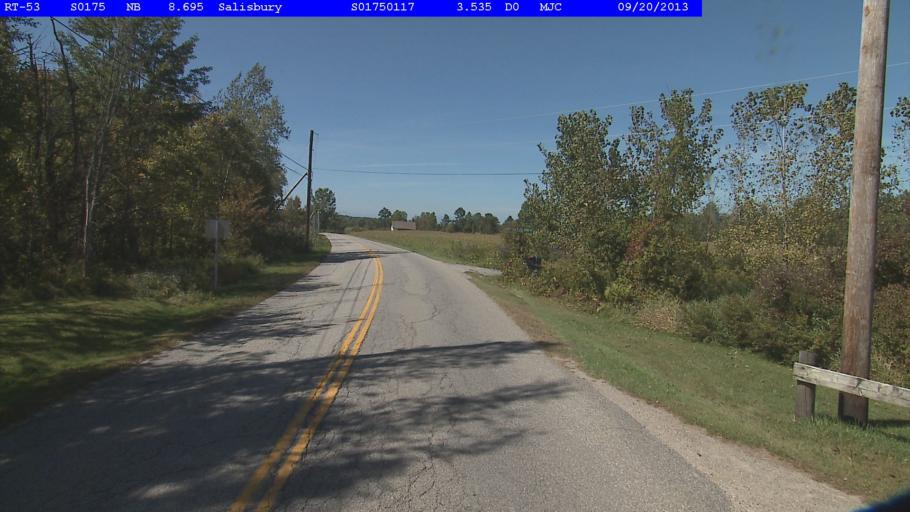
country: US
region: Vermont
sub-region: Addison County
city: Middlebury (village)
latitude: 43.9262
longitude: -73.0990
